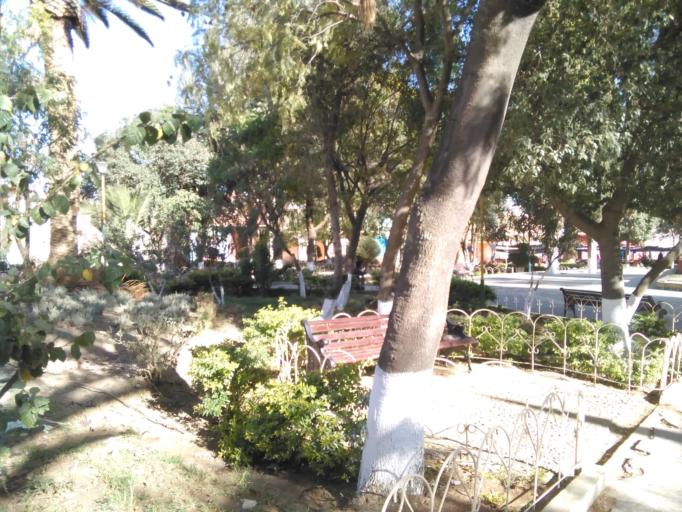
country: BO
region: Cochabamba
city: Punata
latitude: -17.5227
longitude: -65.8942
